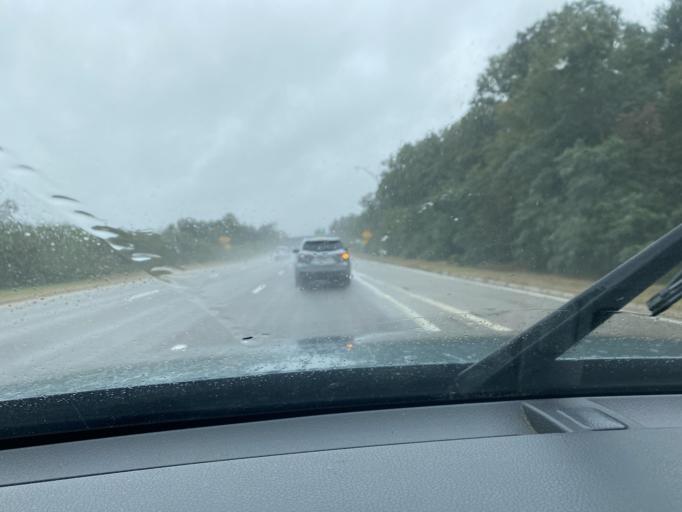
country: US
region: Massachusetts
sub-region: Bristol County
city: Raynham Center
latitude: 41.9518
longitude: -71.0249
